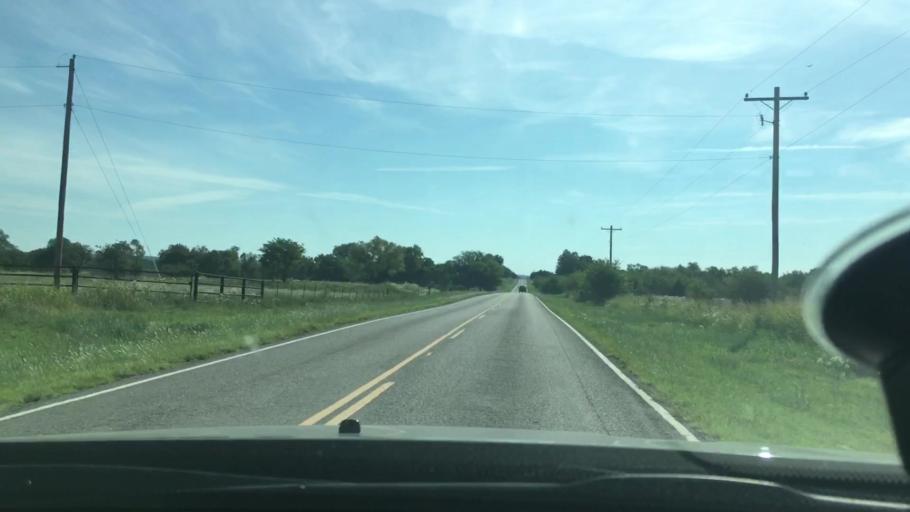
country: US
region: Oklahoma
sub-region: Carter County
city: Ardmore
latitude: 34.3327
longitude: -97.1910
